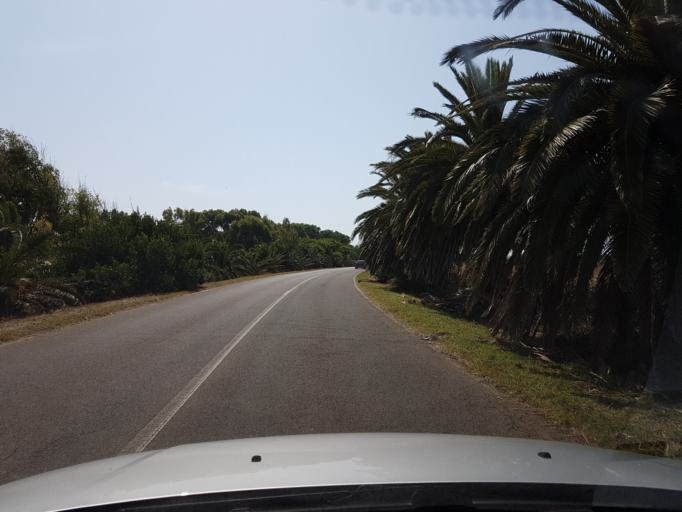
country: IT
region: Sardinia
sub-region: Provincia di Oristano
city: Cabras
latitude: 39.9501
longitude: 8.4160
